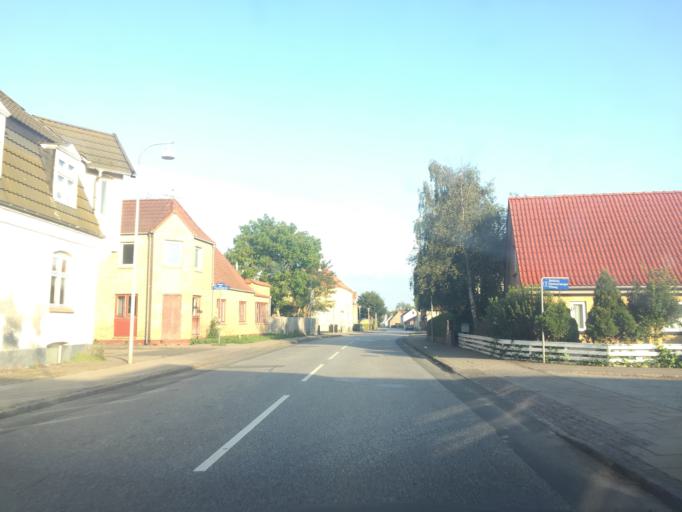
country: DK
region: Zealand
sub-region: Kalundborg Kommune
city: Gorlev
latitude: 55.6195
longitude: 11.2111
